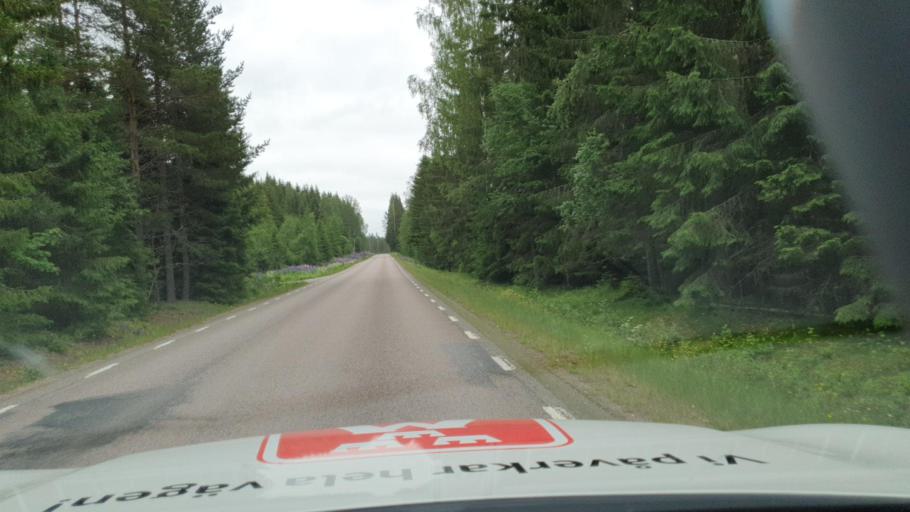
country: SE
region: Vaermland
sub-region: Torsby Kommun
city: Torsby
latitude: 59.9234
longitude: 12.8680
